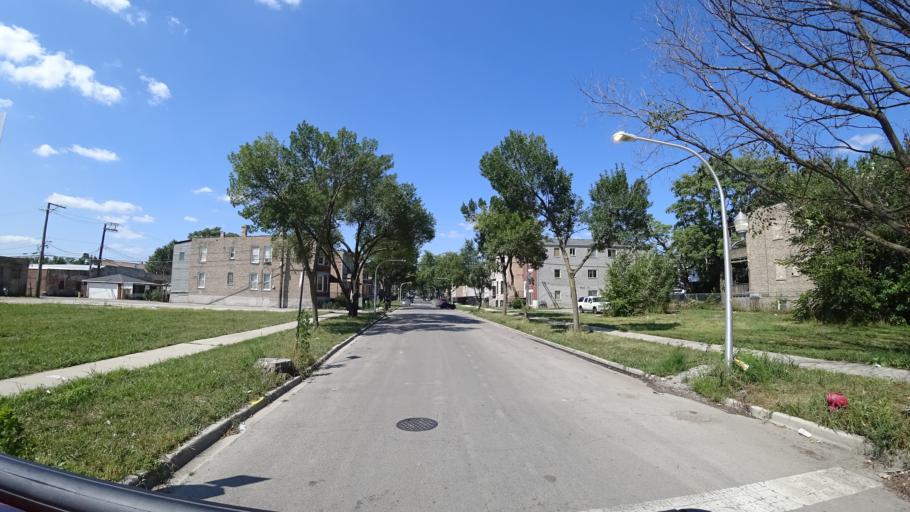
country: US
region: Illinois
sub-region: Cook County
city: Cicero
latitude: 41.8671
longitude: -87.7204
